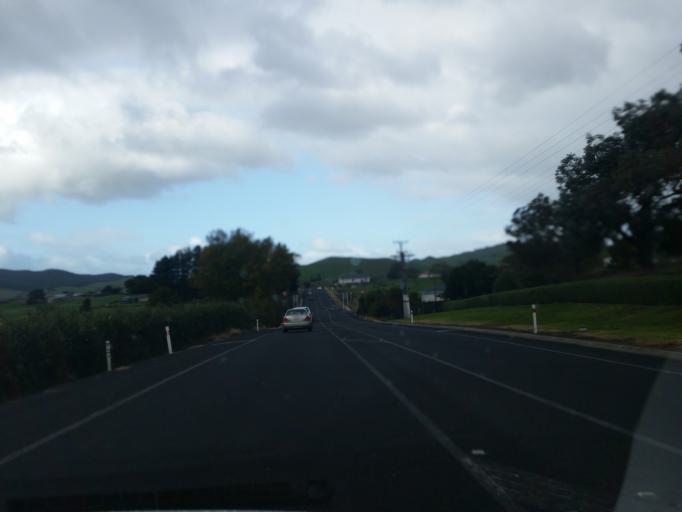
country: NZ
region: Waikato
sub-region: Waikato District
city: Te Kauwhata
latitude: -37.2503
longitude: 175.2281
